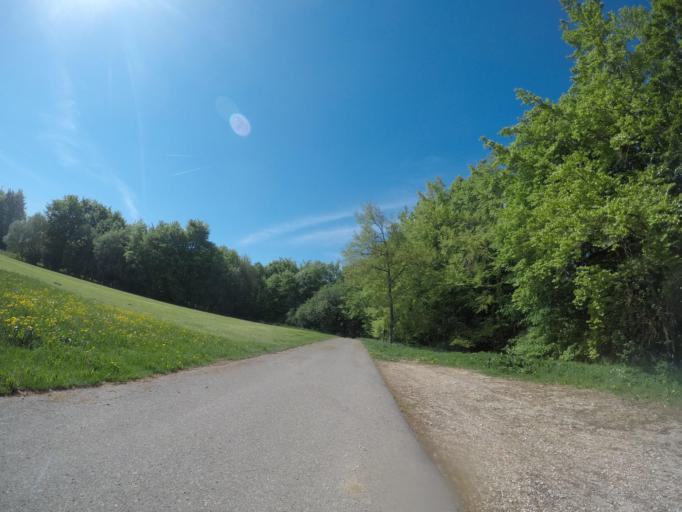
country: DE
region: Baden-Wuerttemberg
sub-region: Tuebingen Region
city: Laichingen
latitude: 48.4343
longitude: 9.6842
